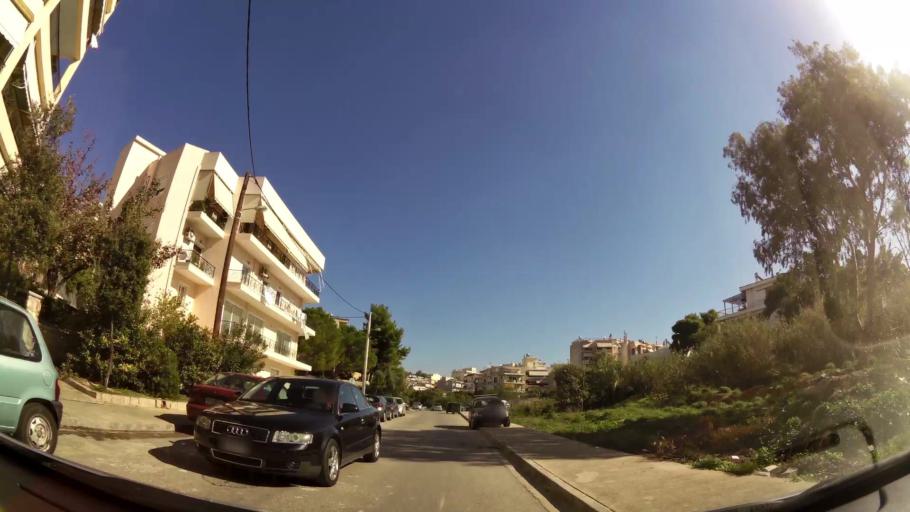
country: GR
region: Attica
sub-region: Nomarchia Athinas
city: Metamorfosi
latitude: 38.0604
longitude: 23.7660
